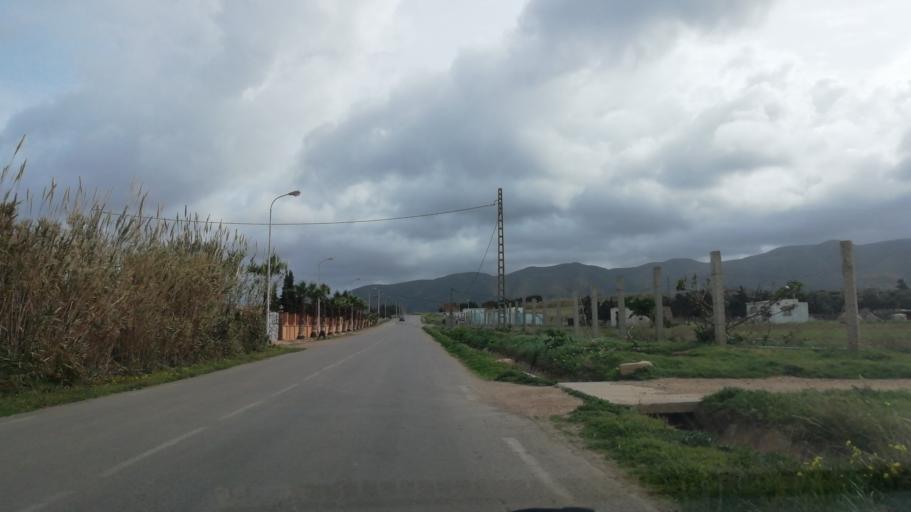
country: DZ
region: Oran
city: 'Ain el Turk
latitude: 35.7004
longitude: -0.8861
